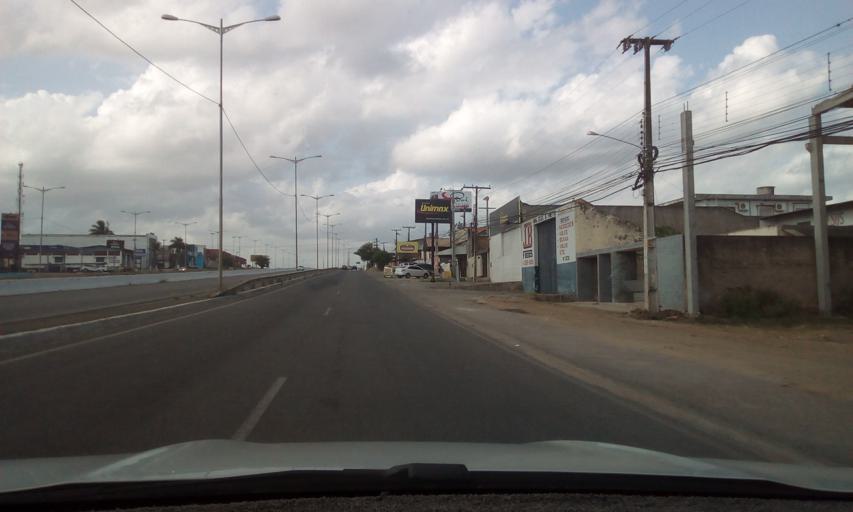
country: BR
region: Pernambuco
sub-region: Caruaru
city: Caruaru
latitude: -8.2575
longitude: -35.9754
